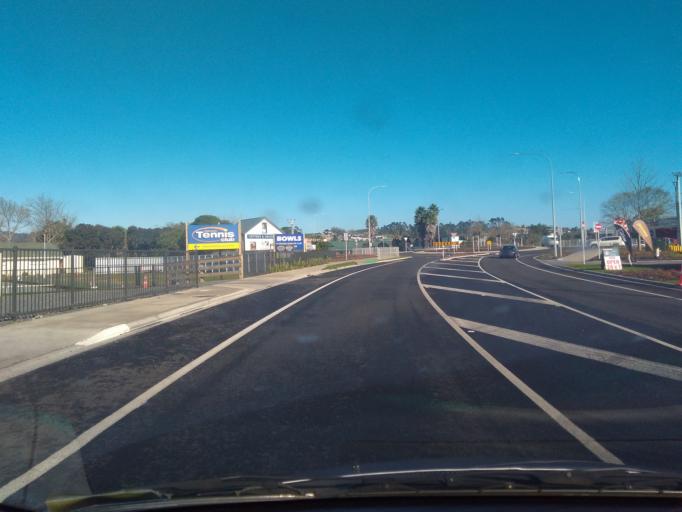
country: NZ
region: Auckland
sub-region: Auckland
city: Muriwai Beach
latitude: -36.7689
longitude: 174.4932
